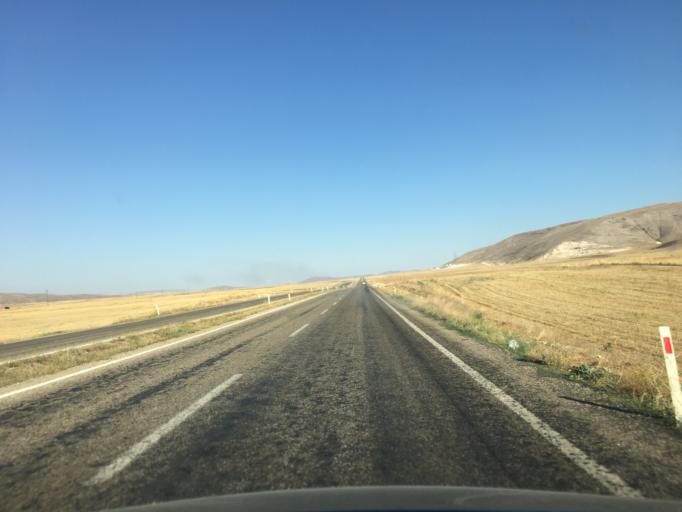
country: TR
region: Kirsehir
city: Akpinar
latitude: 39.3414
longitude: 33.9718
